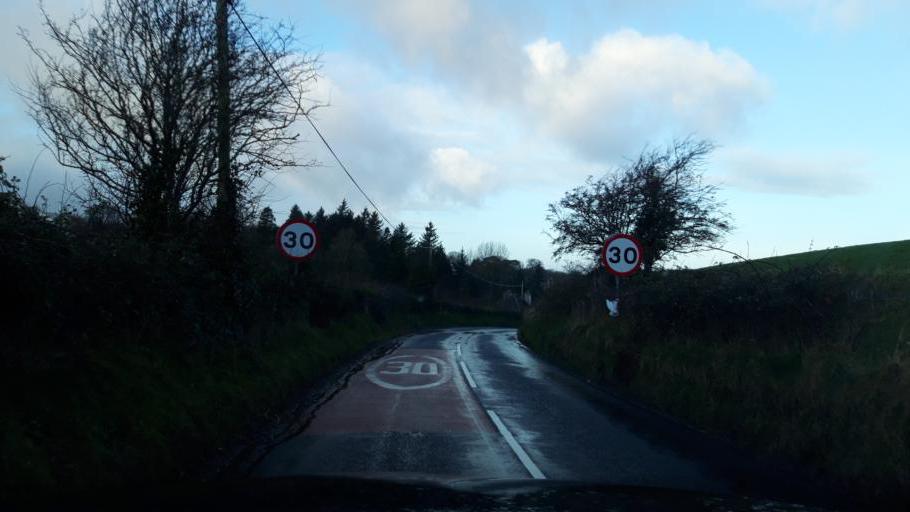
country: GB
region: Northern Ireland
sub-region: Moyle District
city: Ballycastle
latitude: 55.1979
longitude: -6.2297
